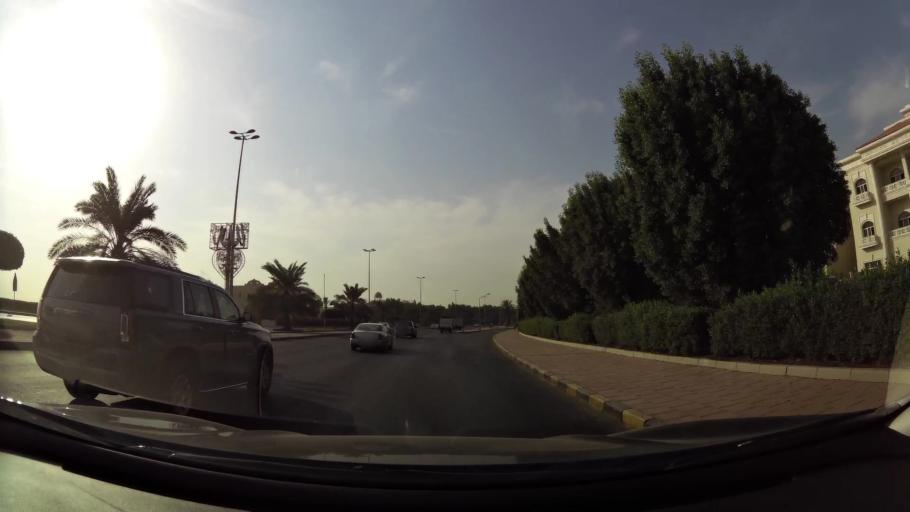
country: KW
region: Muhafazat Hawalli
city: Salwa
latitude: 29.2750
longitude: 48.0887
